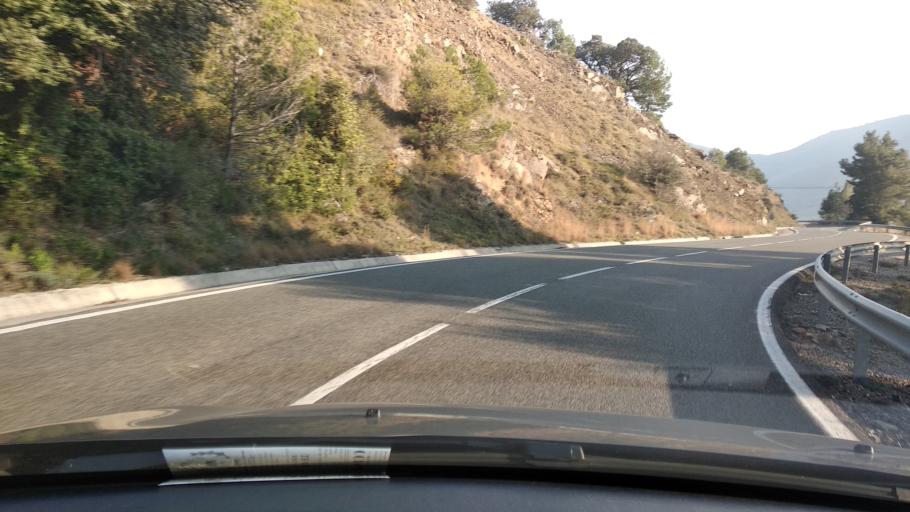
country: ES
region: Catalonia
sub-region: Provincia de Tarragona
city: Alforja
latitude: 41.2200
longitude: 0.9504
